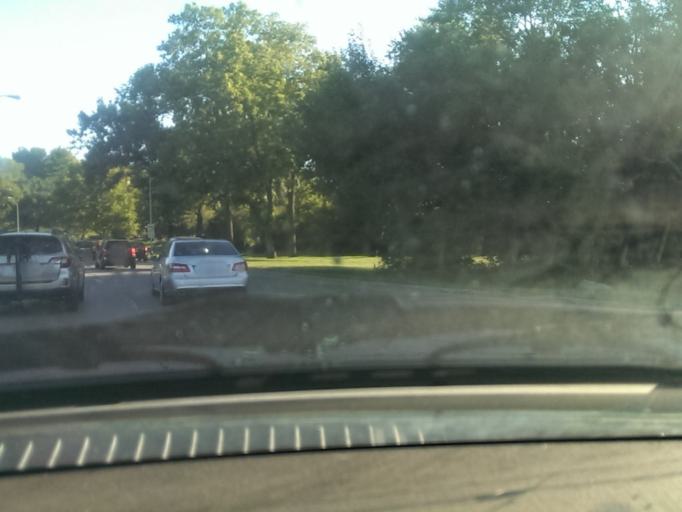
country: US
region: Kansas
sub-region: Johnson County
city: Westwood
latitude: 39.0332
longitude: -94.6057
